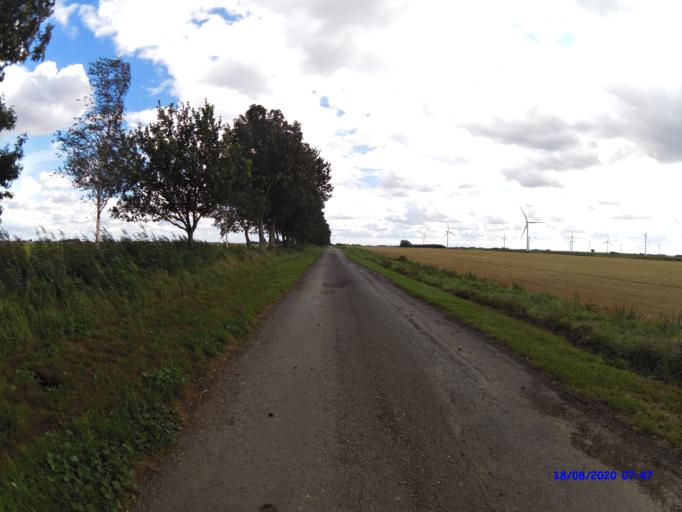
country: GB
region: England
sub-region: Cambridgeshire
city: Whittlesey
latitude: 52.5241
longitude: -0.0995
